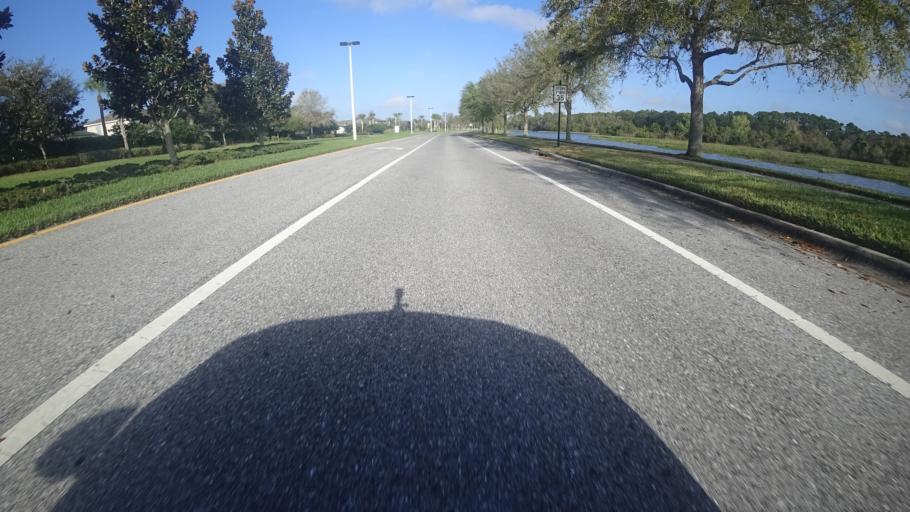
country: US
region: Florida
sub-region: Manatee County
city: Ellenton
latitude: 27.5681
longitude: -82.4634
